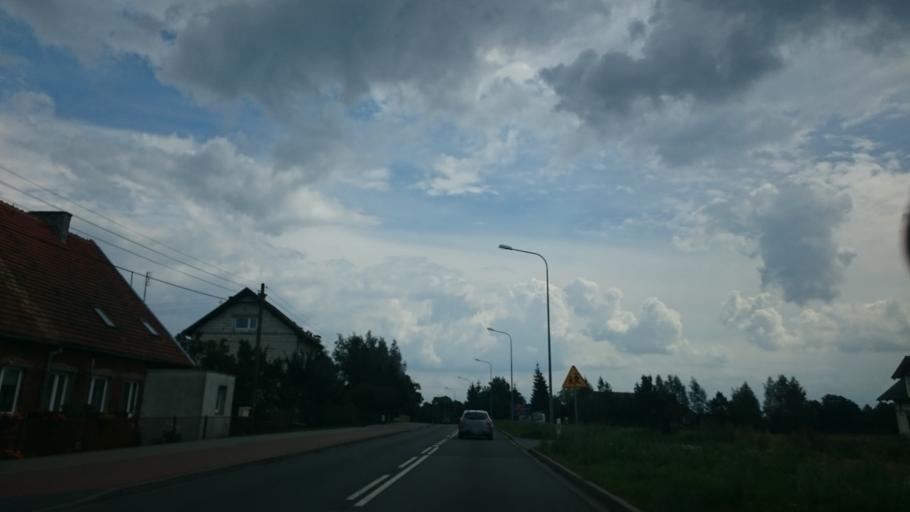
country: PL
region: Kujawsko-Pomorskie
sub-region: Powiat tucholski
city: Kesowo
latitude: 53.6518
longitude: 17.6971
